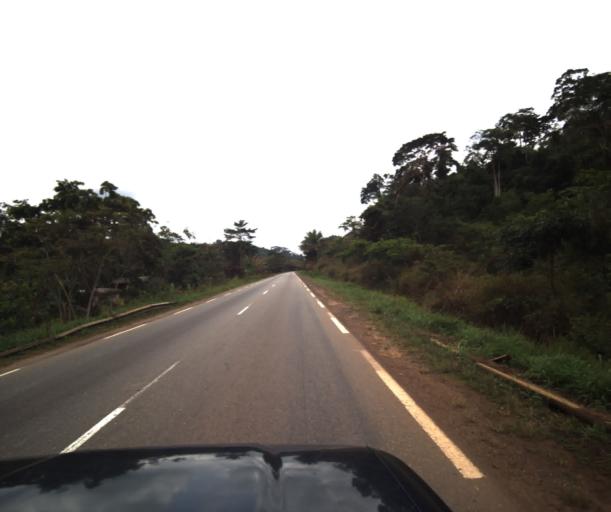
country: CM
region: Centre
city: Eseka
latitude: 3.8336
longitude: 10.9928
